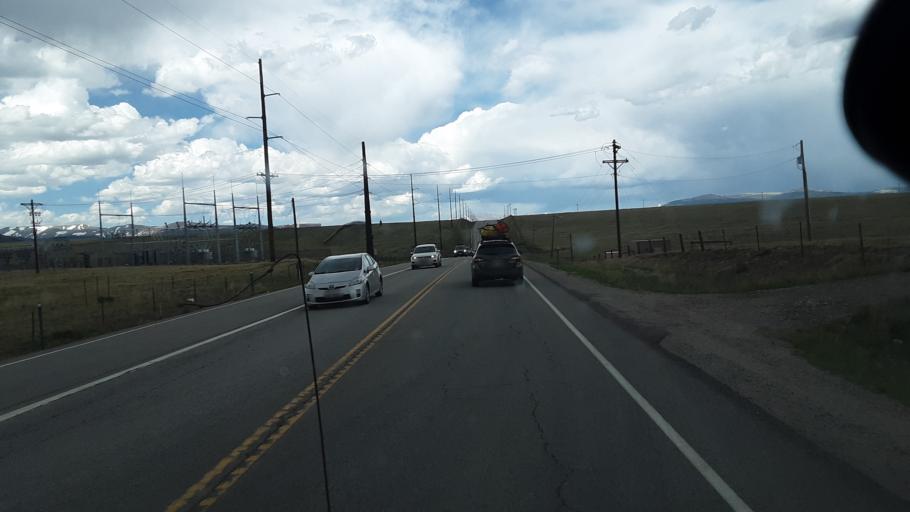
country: US
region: Colorado
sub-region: Park County
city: Fairplay
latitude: 39.3105
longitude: -105.8864
